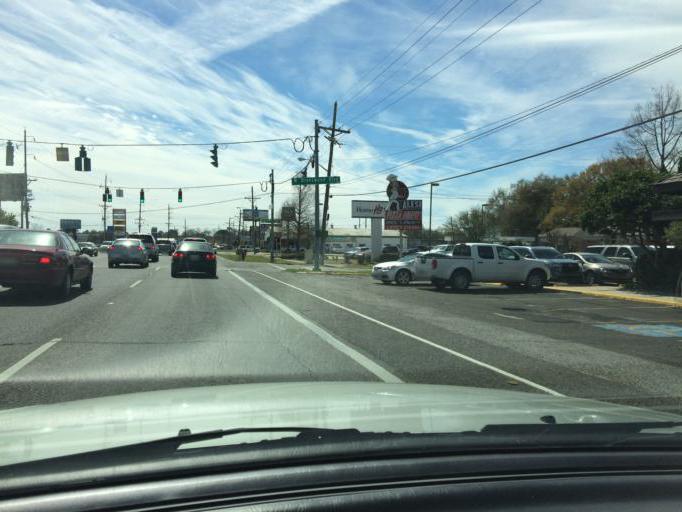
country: US
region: Louisiana
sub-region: Lafayette Parish
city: Lafayette
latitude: 30.1968
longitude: -92.0569
